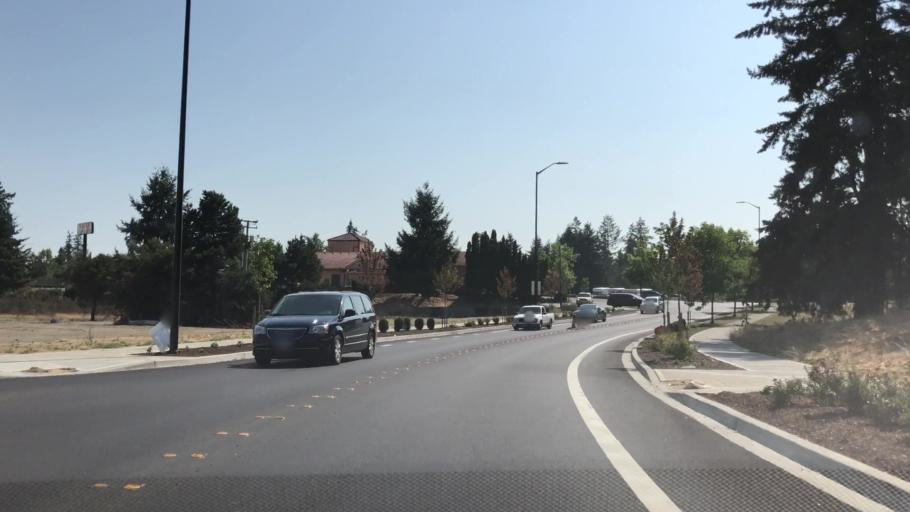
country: US
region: Washington
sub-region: Thurston County
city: Tanglewilde-Thompson Place
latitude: 47.0666
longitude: -122.7649
